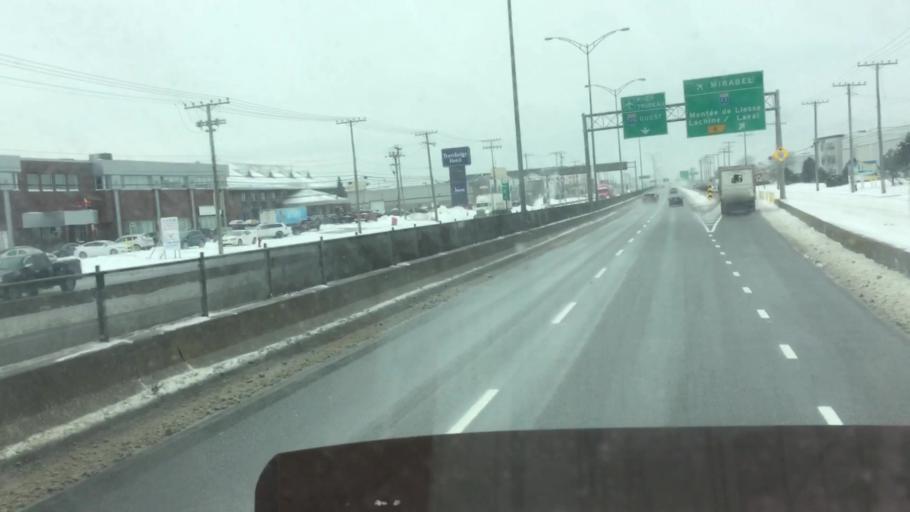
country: CA
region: Quebec
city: Hampstead
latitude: 45.4812
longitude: -73.6979
